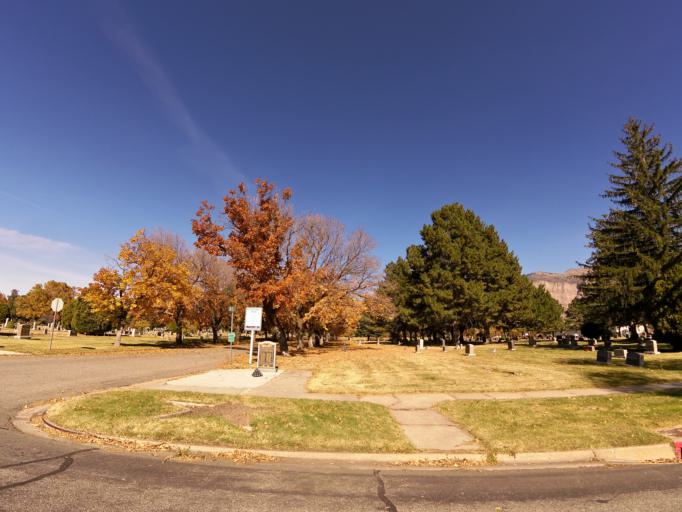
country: US
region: Utah
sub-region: Weber County
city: Ogden
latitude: 41.2310
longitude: -111.9618
